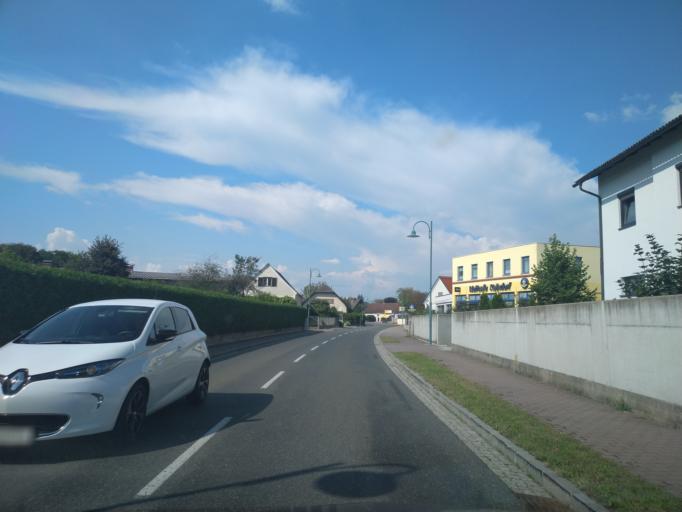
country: AT
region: Styria
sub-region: Politischer Bezirk Leibnitz
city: Kaindorf an der Sulm
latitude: 46.7945
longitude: 15.5383
